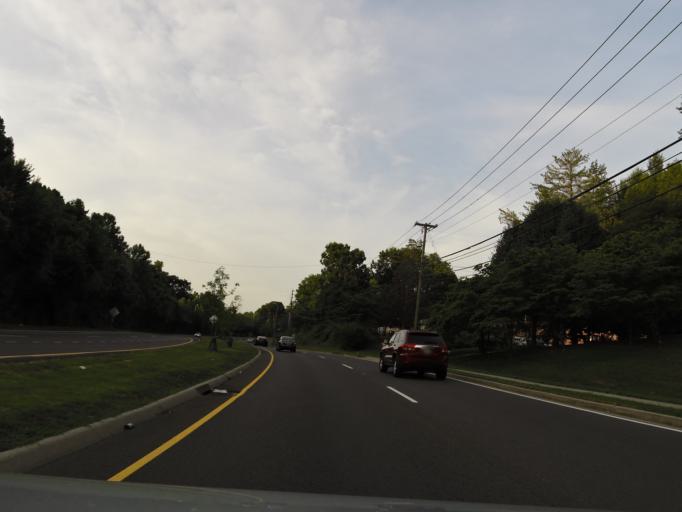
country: US
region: Tennessee
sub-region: Knox County
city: Farragut
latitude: 35.9423
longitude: -84.0590
